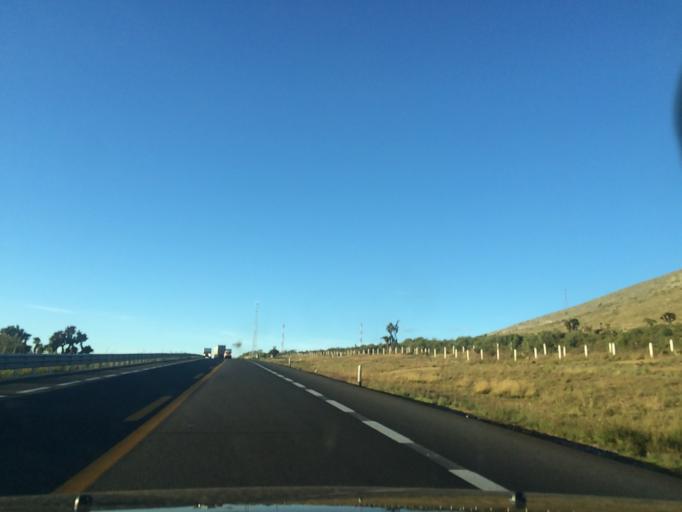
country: MX
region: Puebla
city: Morelos Canada
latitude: 18.7208
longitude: -97.4725
